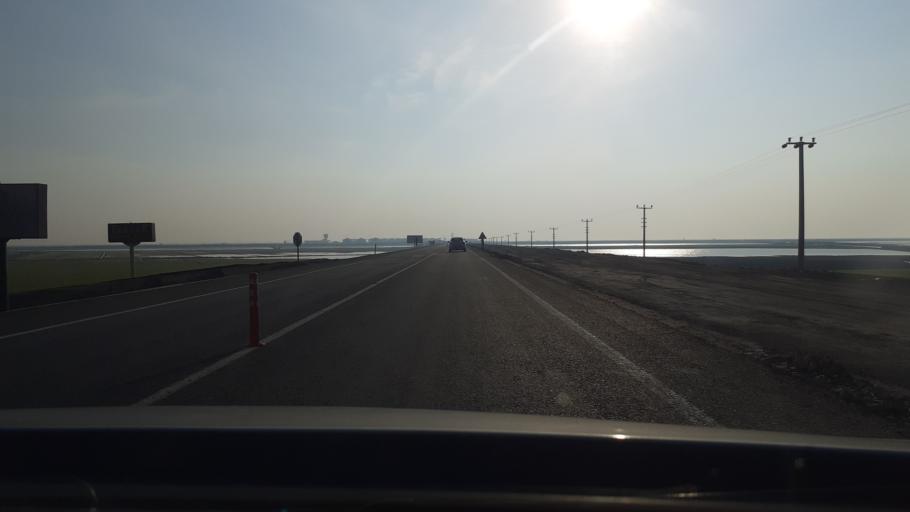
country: TR
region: Hatay
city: Serinyol
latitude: 36.3694
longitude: 36.2568
